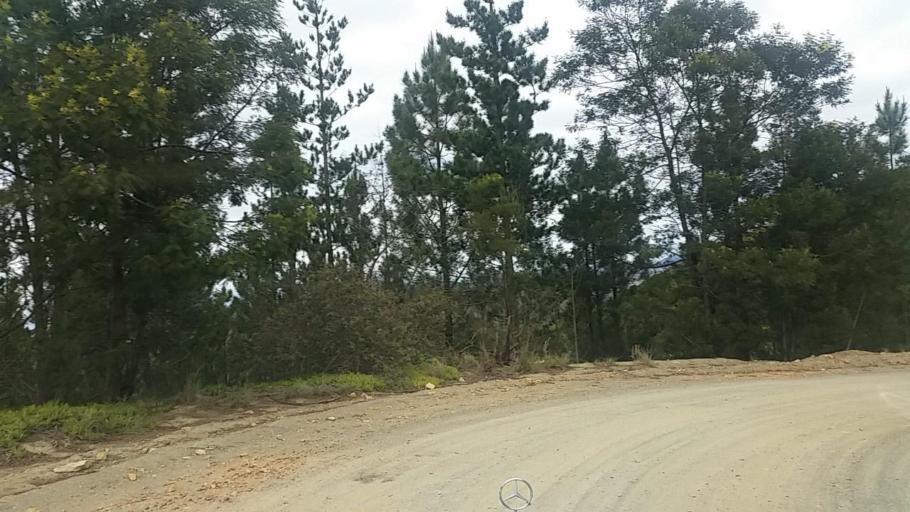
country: ZA
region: Western Cape
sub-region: Eden District Municipality
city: Knysna
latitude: -33.7573
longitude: 23.1576
